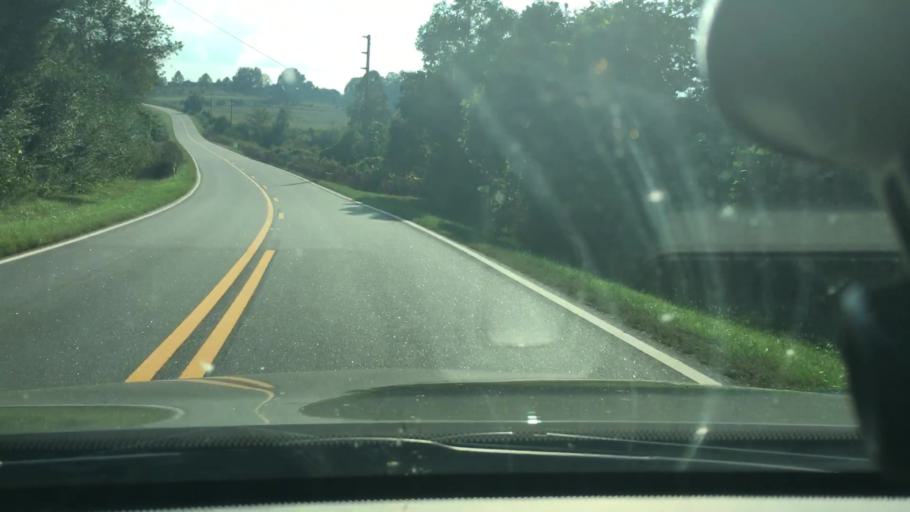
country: US
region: North Carolina
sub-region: Polk County
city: Columbus
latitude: 35.3103
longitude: -82.1483
